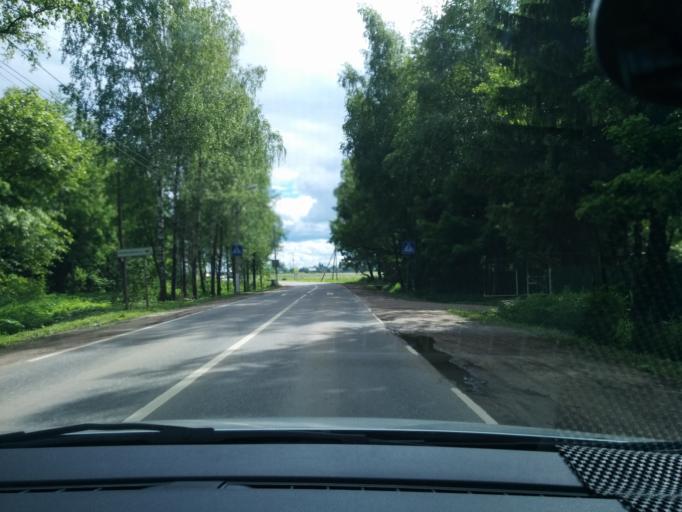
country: RU
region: Moskovskaya
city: Lugovaya
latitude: 56.0361
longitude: 37.4700
